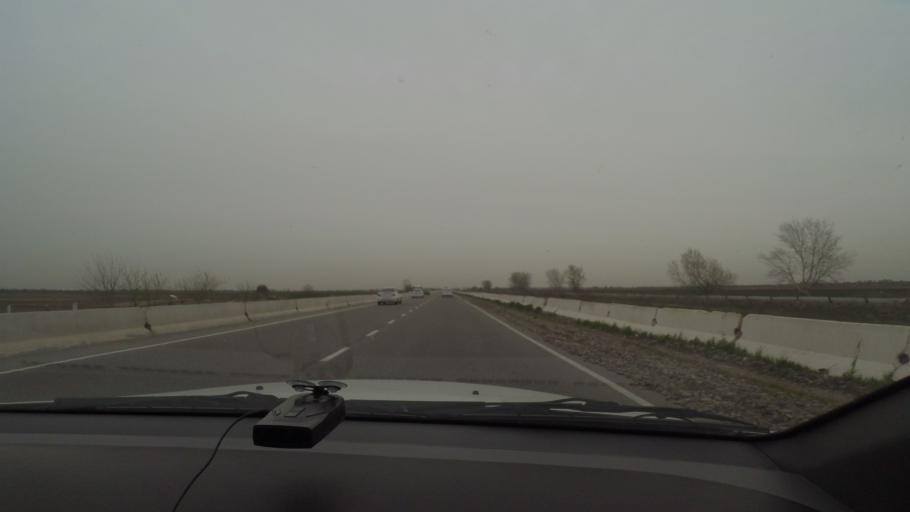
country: UZ
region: Jizzax
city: Gagarin
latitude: 40.4746
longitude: 68.2779
